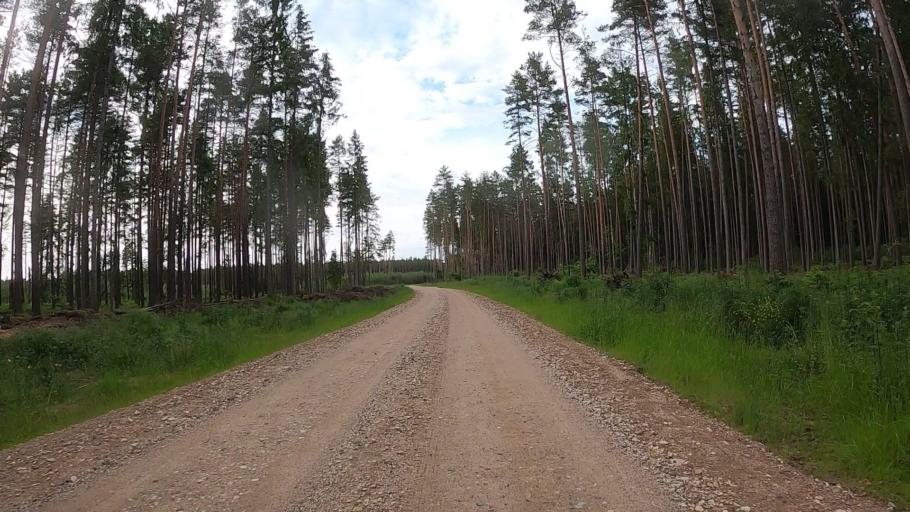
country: LV
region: Olaine
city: Olaine
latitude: 56.7670
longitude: 23.9033
